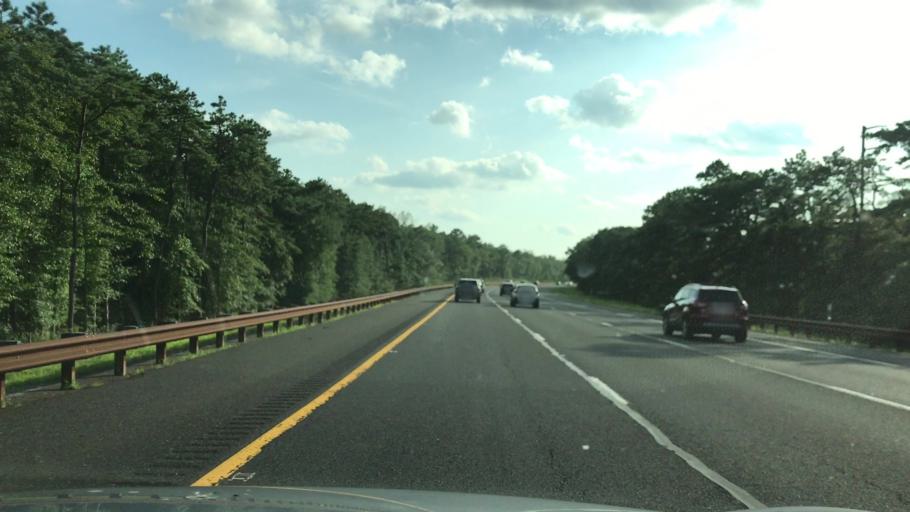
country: US
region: New Jersey
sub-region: Ocean County
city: Tuckerton
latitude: 39.6586
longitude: -74.3327
